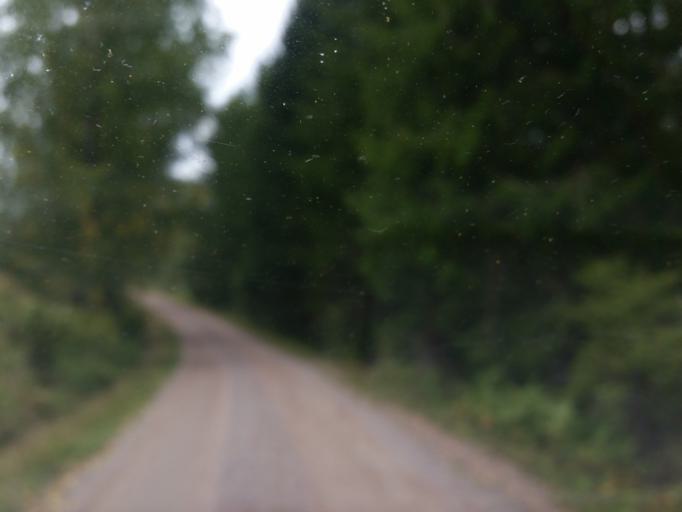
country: SE
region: Dalarna
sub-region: Leksand Municipality
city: Smedby
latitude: 60.6684
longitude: 15.1296
